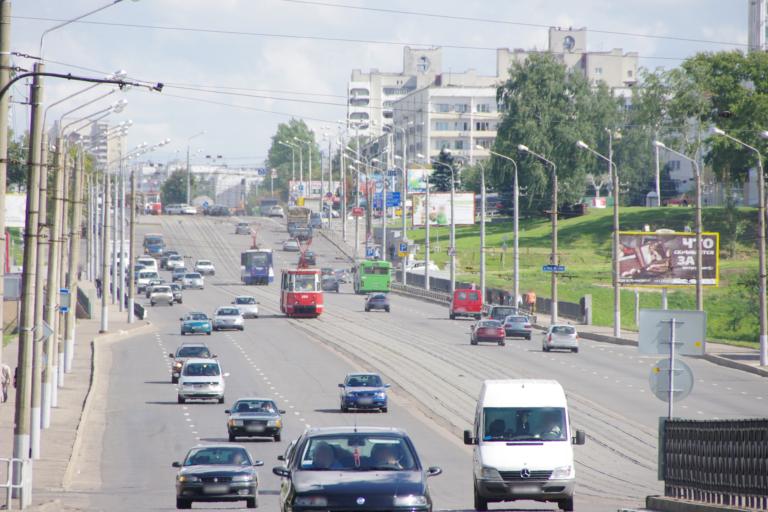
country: BY
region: Vitebsk
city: Vitebsk
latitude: 55.1858
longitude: 30.1884
